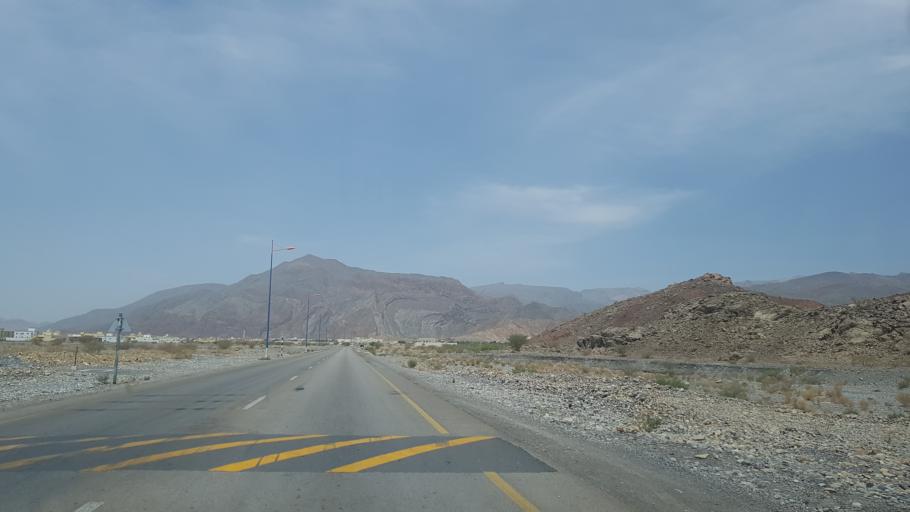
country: OM
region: Muhafazat ad Dakhiliyah
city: Izki
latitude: 22.8953
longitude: 57.6836
